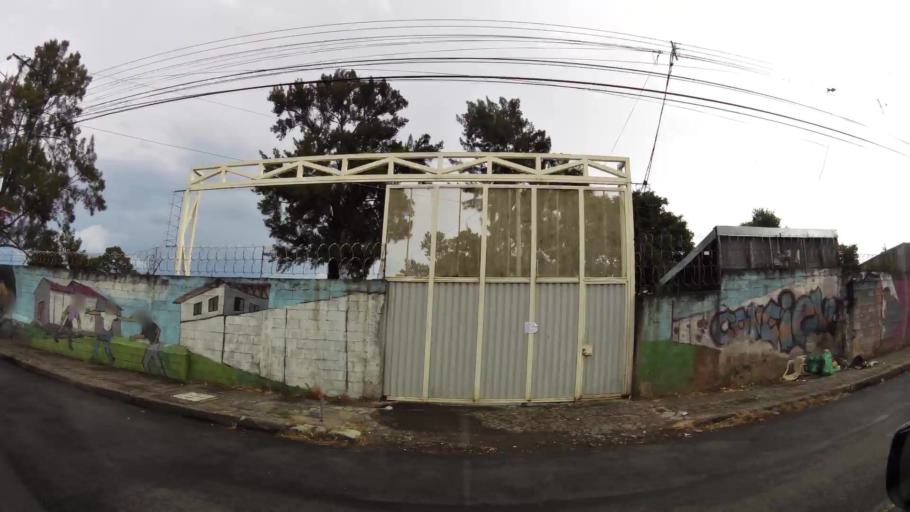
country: CR
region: San Jose
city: Colima
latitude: 9.9418
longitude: -84.0910
